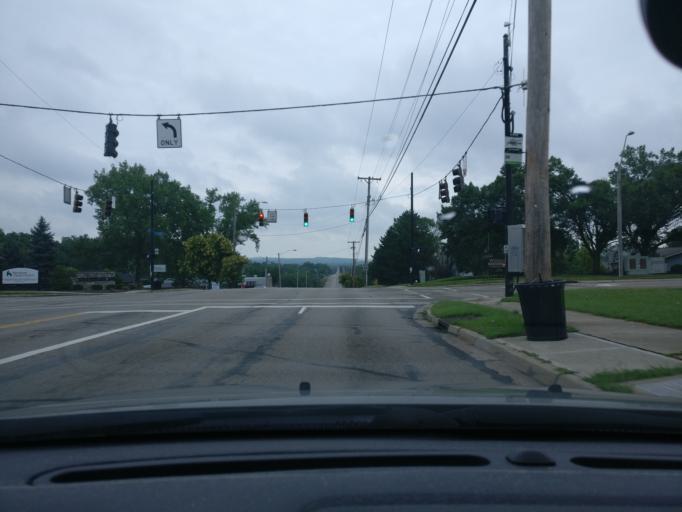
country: US
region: Ohio
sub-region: Montgomery County
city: West Carrollton City
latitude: 39.6477
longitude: -84.2429
